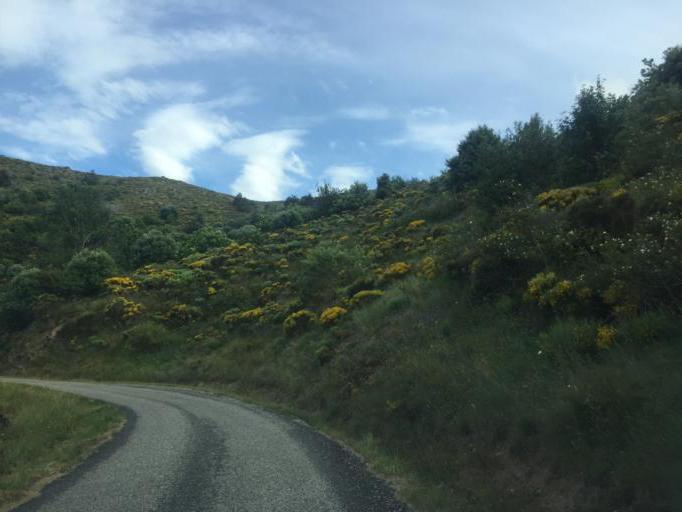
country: FR
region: Rhone-Alpes
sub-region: Departement de l'Ardeche
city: Saint-Julien-en-Saint-Alban
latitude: 44.7944
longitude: 4.6747
